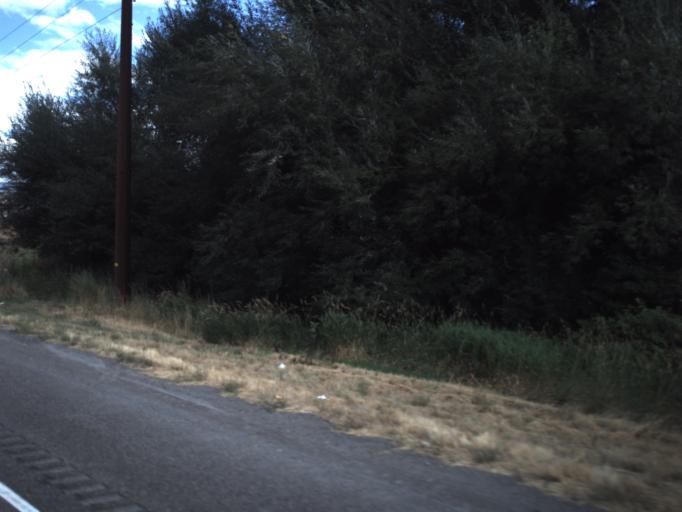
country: US
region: Utah
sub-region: Cache County
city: Wellsville
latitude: 41.6422
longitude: -111.9159
